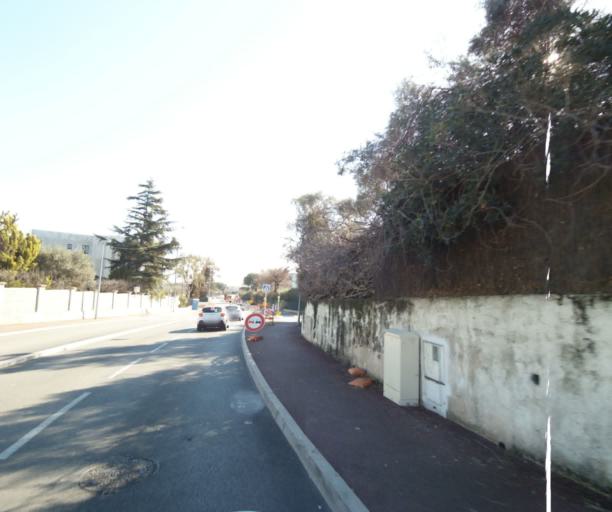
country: FR
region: Provence-Alpes-Cote d'Azur
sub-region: Departement des Alpes-Maritimes
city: Biot
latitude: 43.5940
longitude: 7.1103
